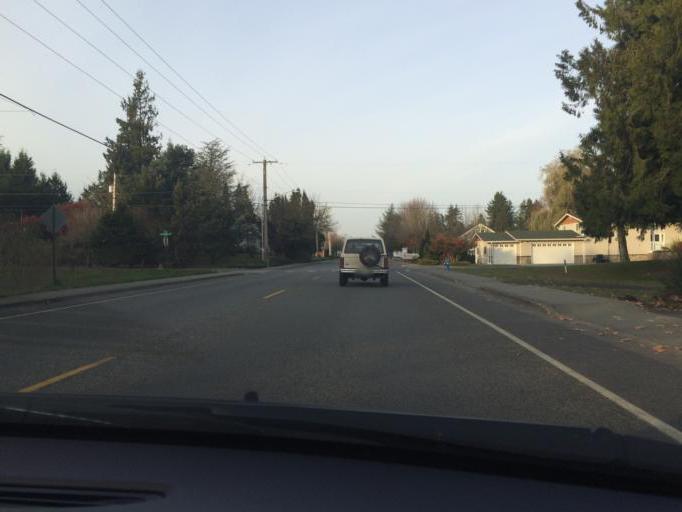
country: US
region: Washington
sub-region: Whatcom County
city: Lynden
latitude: 48.9501
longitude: -122.4522
